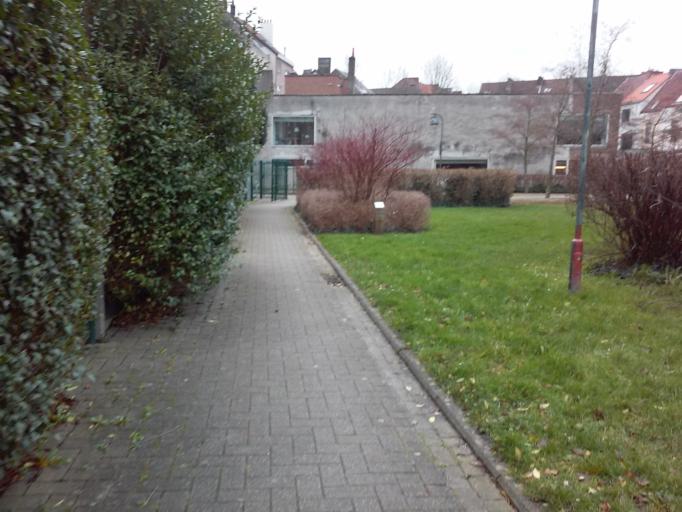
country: BE
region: Flanders
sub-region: Provincie Oost-Vlaanderen
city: Ledeberg
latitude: 51.0515
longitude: 3.7402
